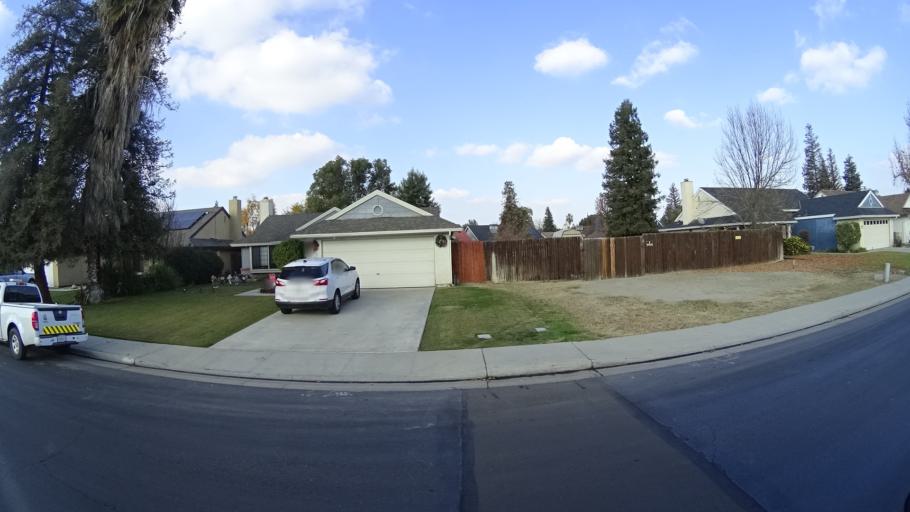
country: US
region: California
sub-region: Kern County
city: Greenacres
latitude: 35.3123
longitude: -119.1069
